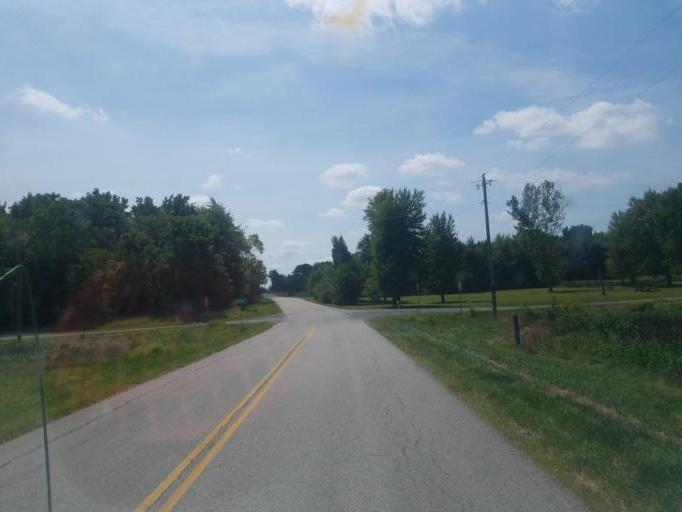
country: US
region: Ohio
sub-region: Union County
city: Marysville
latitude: 40.3057
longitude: -83.2945
